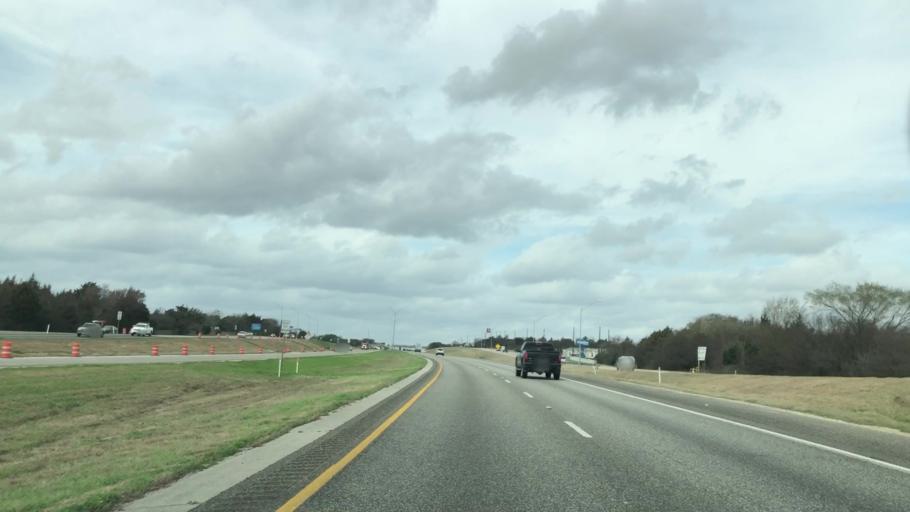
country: US
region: Texas
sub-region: Brazos County
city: Bryan
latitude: 30.6902
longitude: -96.3514
